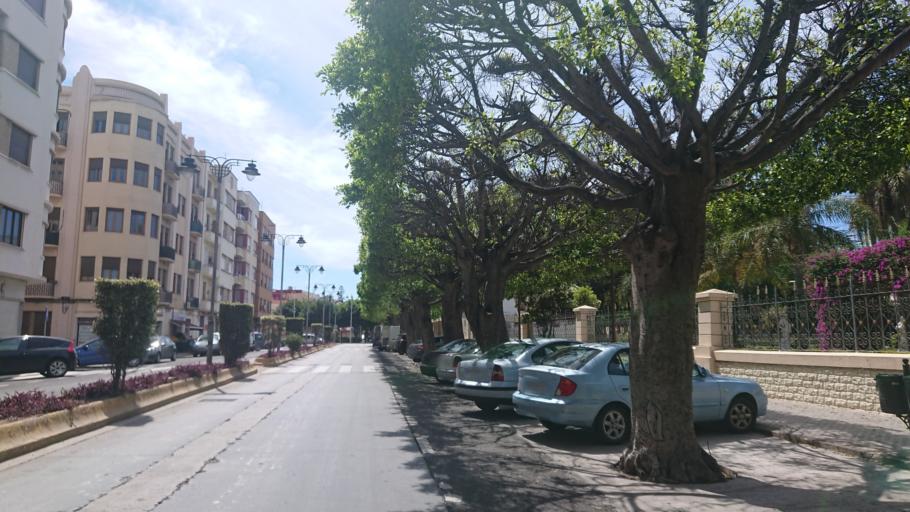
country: ES
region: Melilla
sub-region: Melilla
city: Melilla
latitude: 35.2912
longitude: -2.9410
